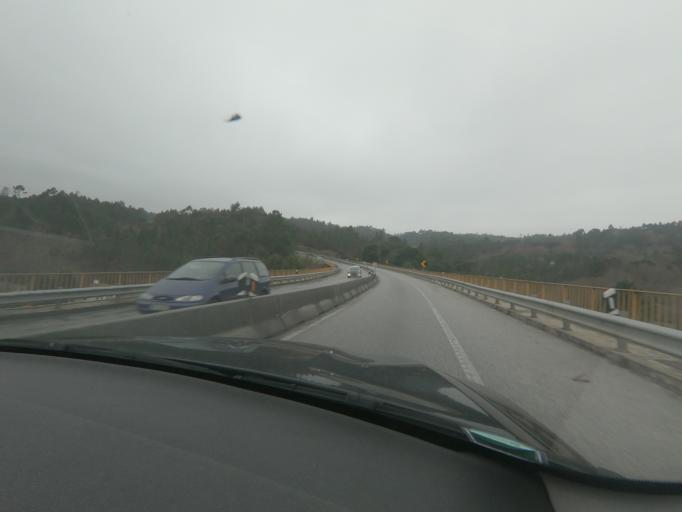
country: PT
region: Viseu
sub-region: Viseu
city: Viseu
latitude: 40.6018
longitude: -7.9936
